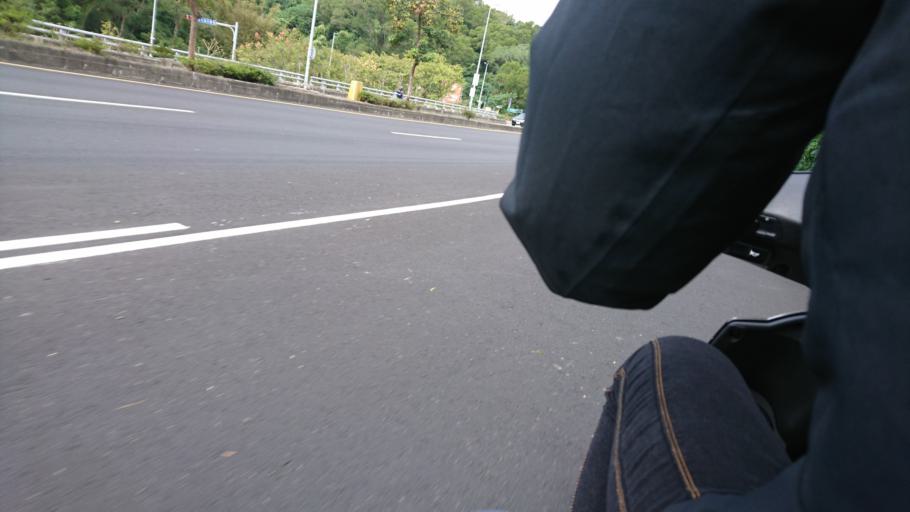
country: TW
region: Taiwan
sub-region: Hsinchu
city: Hsinchu
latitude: 24.7739
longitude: 120.9533
